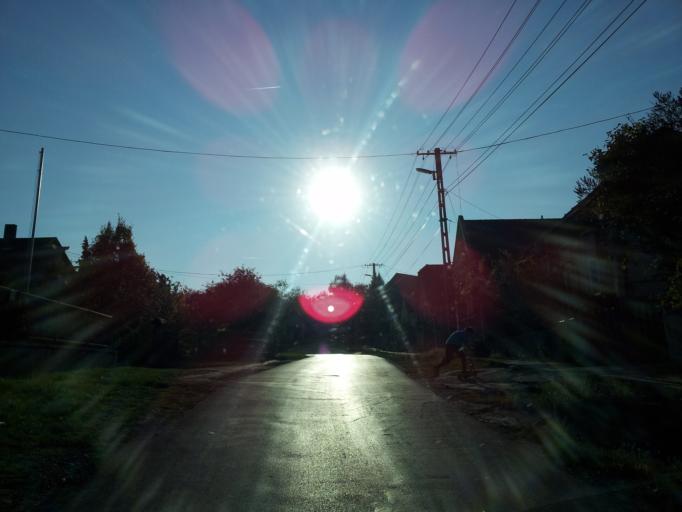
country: HU
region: Fejer
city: Fehervarcsurgo
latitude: 47.2913
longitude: 18.2631
